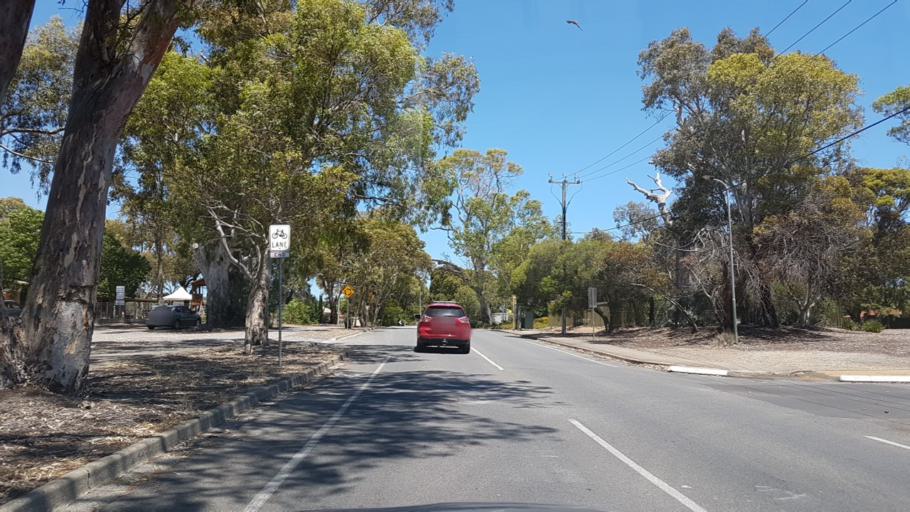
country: AU
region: South Australia
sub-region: Marion
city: Trott Park
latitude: -35.0918
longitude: 138.5593
